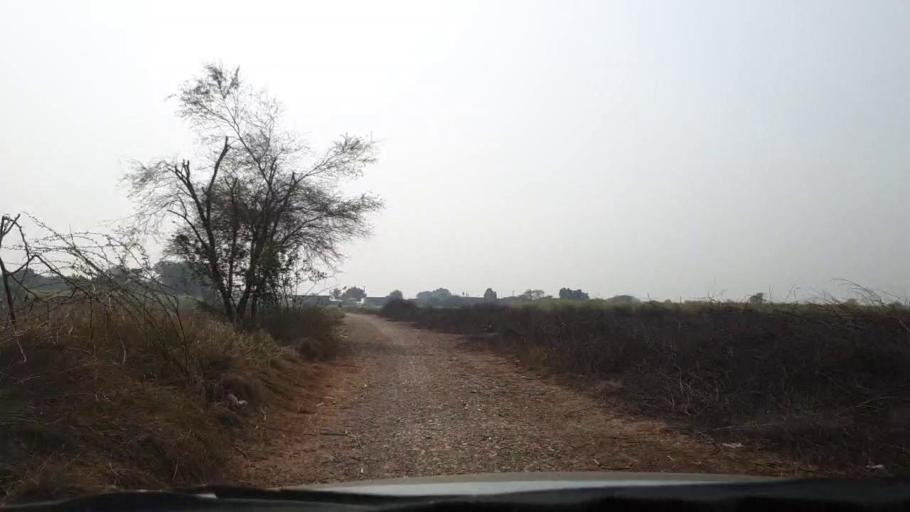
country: PK
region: Sindh
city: Matiari
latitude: 25.6351
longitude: 68.5151
